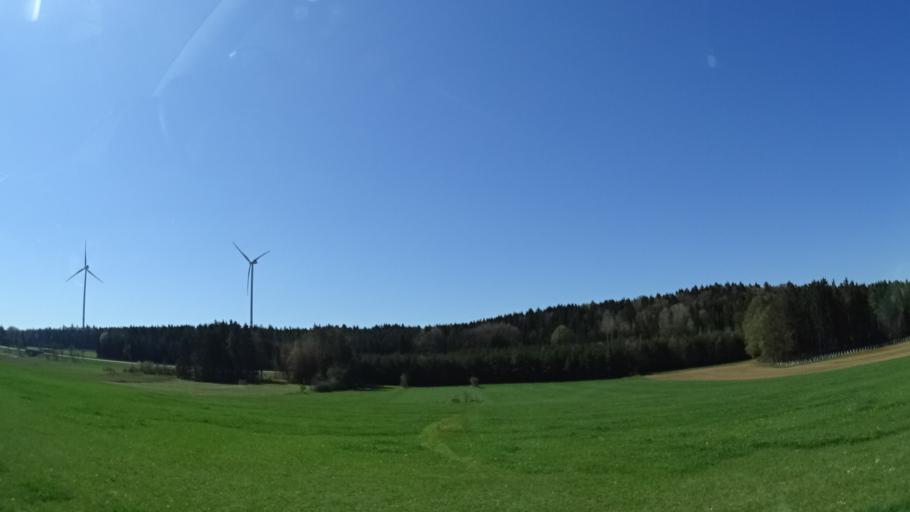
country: DE
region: Bavaria
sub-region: Regierungsbezirk Mittelfranken
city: Alfeld
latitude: 49.4118
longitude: 11.5769
